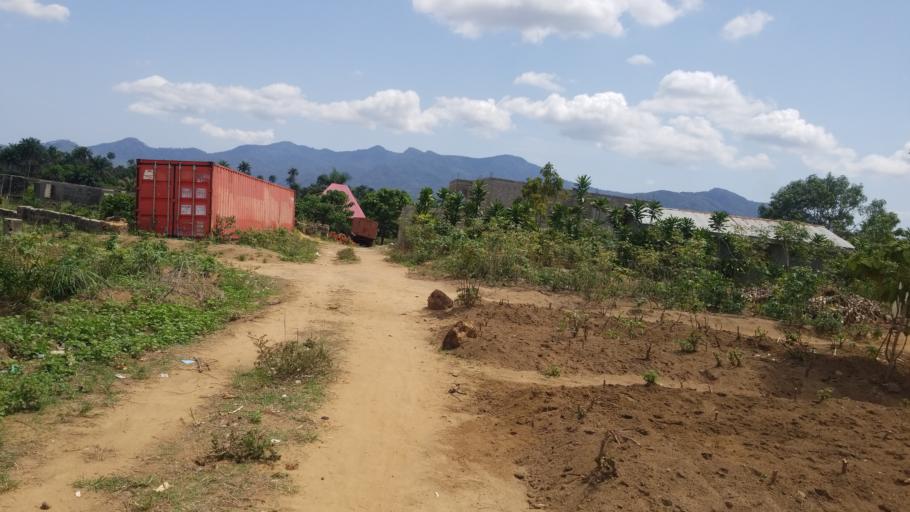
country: SL
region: Western Area
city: Waterloo
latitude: 8.3105
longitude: -13.0570
